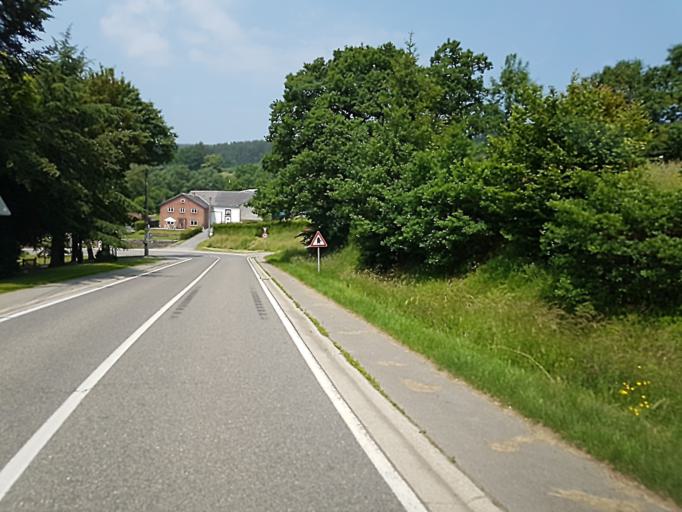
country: BE
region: Wallonia
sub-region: Province de Liege
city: Lierneux
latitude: 50.3289
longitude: 5.7631
